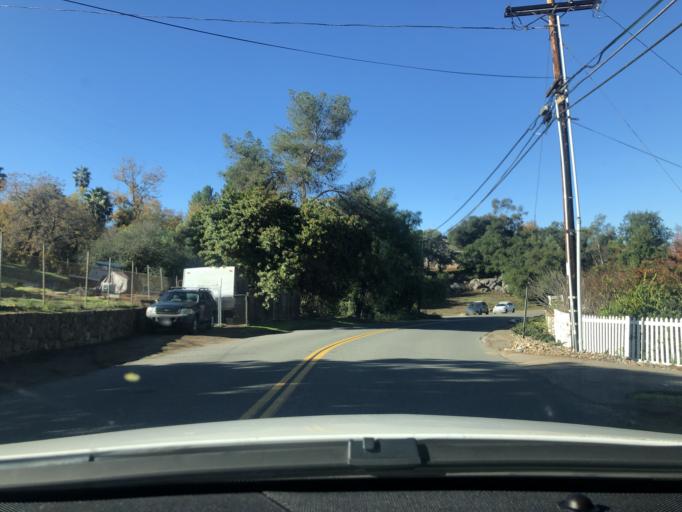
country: US
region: California
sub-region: San Diego County
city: Rancho San Diego
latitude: 32.7751
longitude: -116.9401
